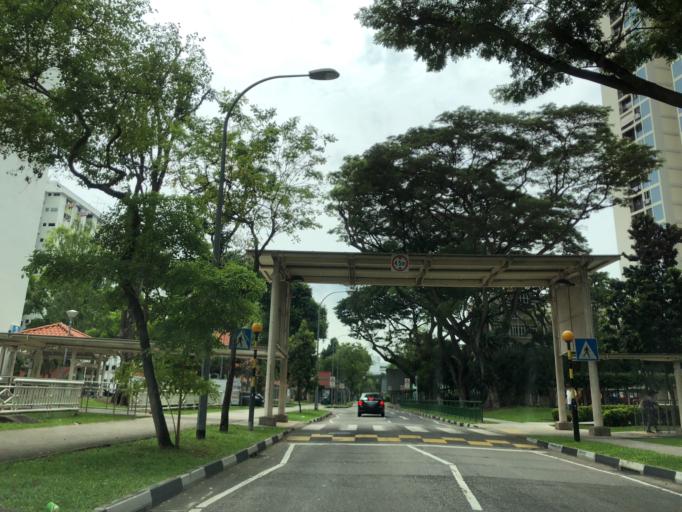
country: SG
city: Singapore
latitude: 1.3138
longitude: 103.8510
